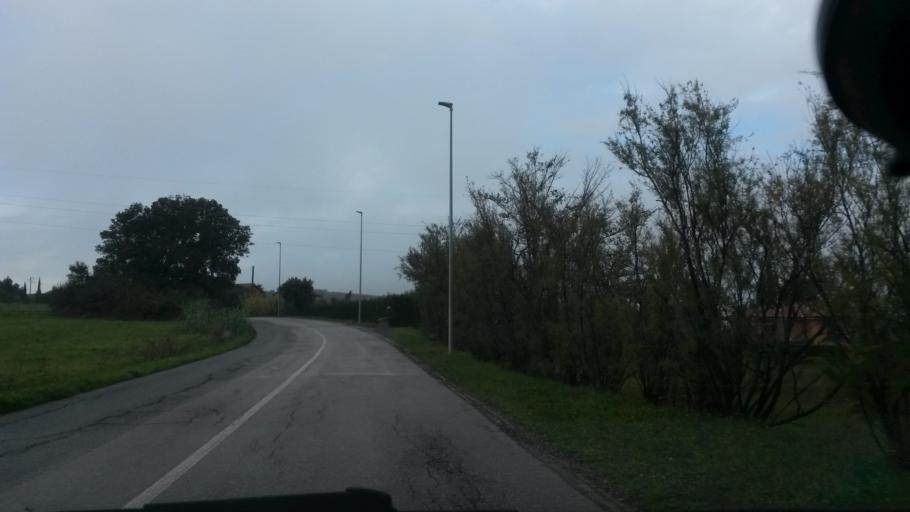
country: IT
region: Tuscany
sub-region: Provincia di Livorno
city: Rosignano Marittimo
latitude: 43.4166
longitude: 10.4625
